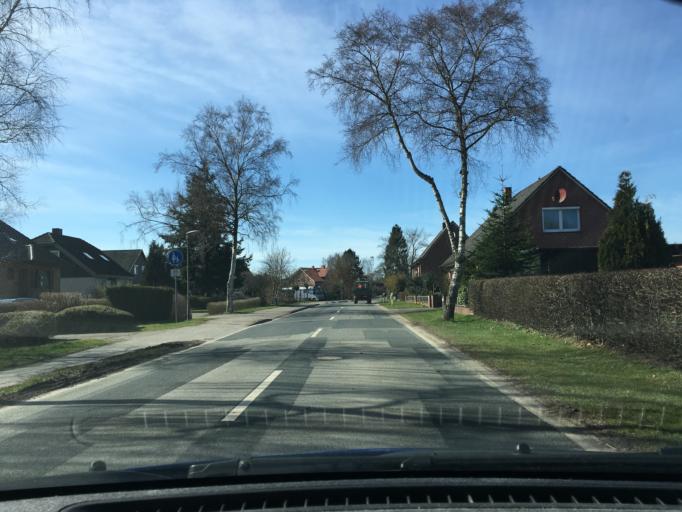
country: DE
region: Lower Saxony
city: Winsen
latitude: 53.3871
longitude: 10.2351
